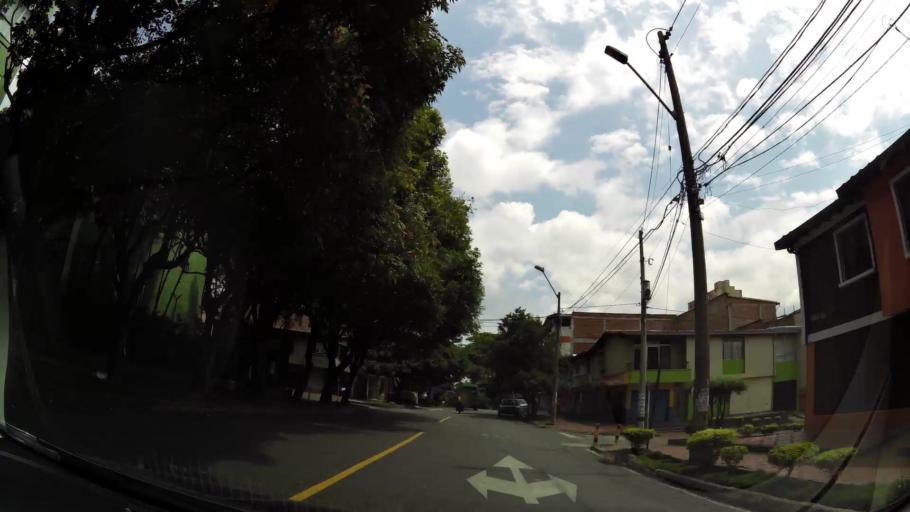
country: CO
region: Antioquia
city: Medellin
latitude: 6.2517
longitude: -75.6107
